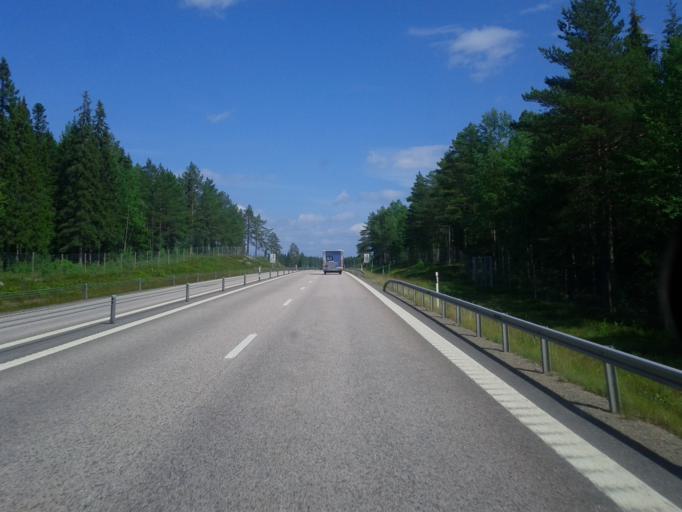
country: SE
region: Vaesterbotten
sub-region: Nordmalings Kommun
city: Nordmaling
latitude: 63.5061
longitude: 19.3483
